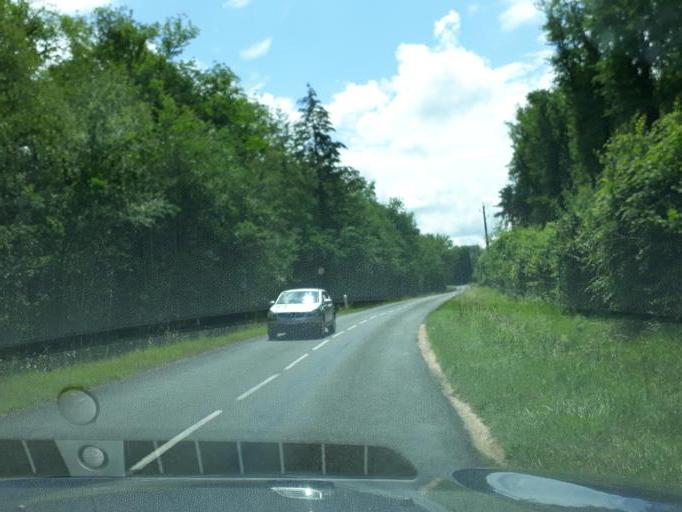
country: FR
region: Centre
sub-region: Departement du Loiret
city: Ligny-le-Ribault
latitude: 47.6601
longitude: 1.8201
